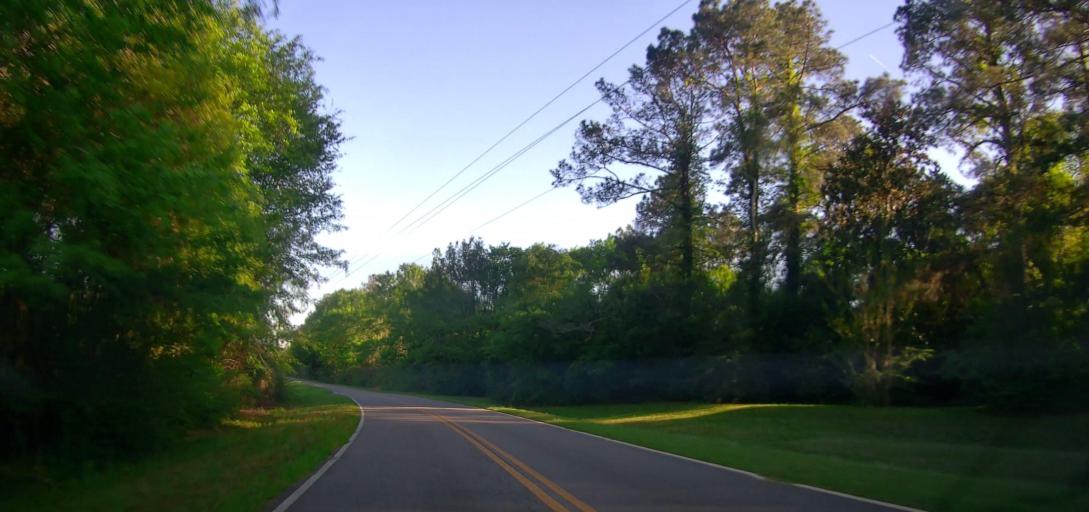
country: US
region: Georgia
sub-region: Macon County
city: Oglethorpe
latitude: 32.2791
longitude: -84.0909
